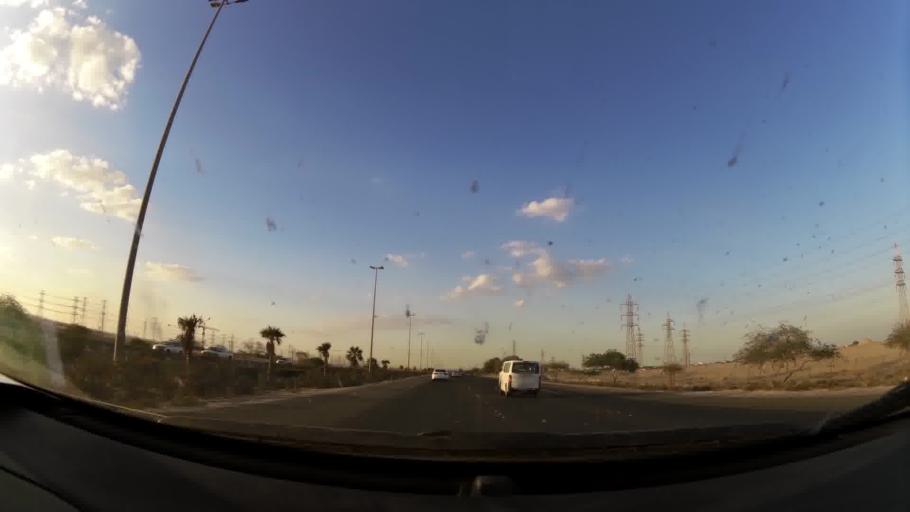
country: KW
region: Al Ahmadi
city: Al Fahahil
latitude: 28.8893
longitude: 48.2248
